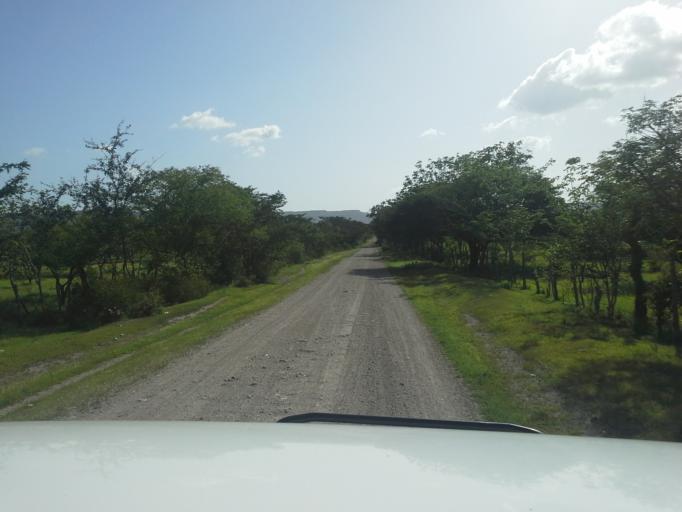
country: NI
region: Matagalpa
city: Ciudad Dario
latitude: 12.6637
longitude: -86.0603
